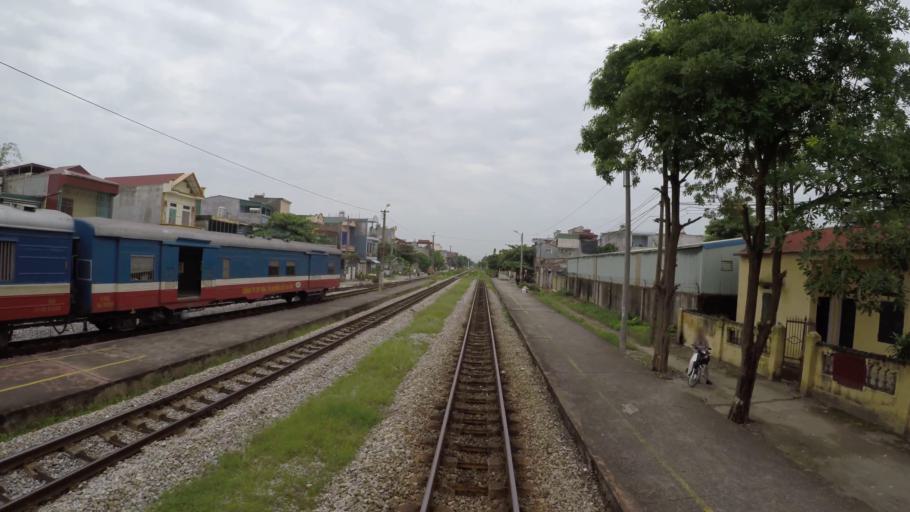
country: VN
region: Hai Duong
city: Thanh Pho Hai Duong
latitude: 20.9426
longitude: 106.3024
